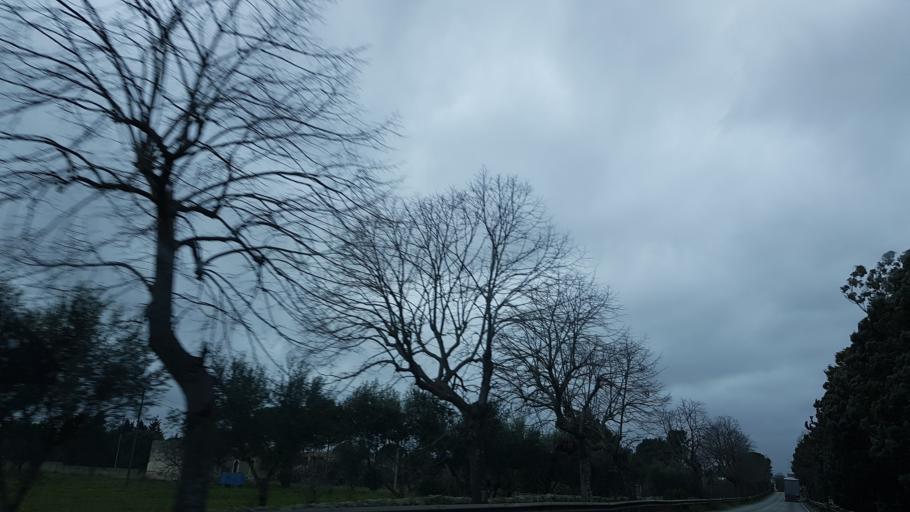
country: IT
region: Apulia
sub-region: Provincia di Brindisi
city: San Vito dei Normanni
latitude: 40.6573
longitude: 17.7250
